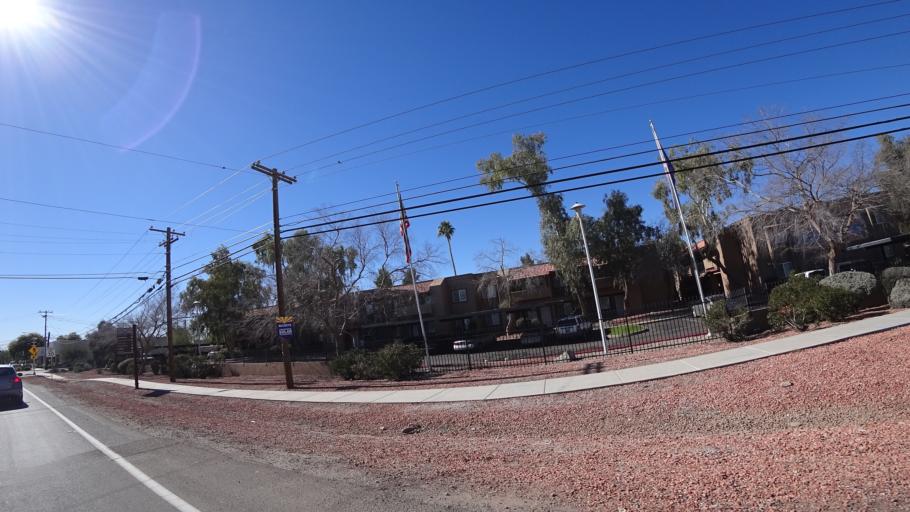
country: US
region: Arizona
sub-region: Maricopa County
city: Buckeye
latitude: 33.3749
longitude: -112.5731
